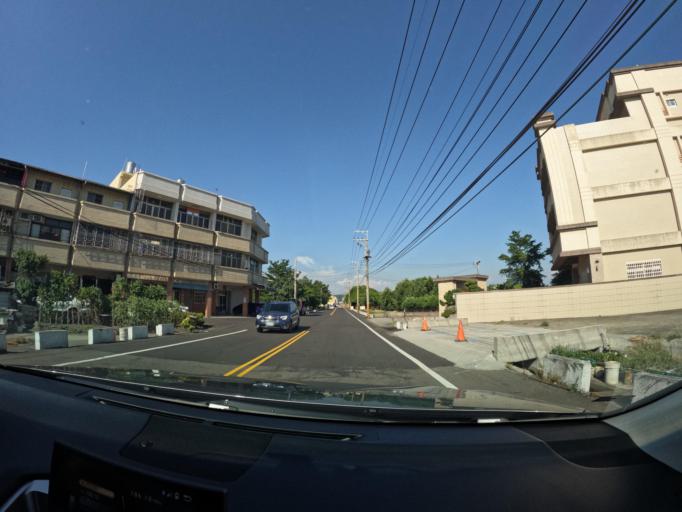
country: TW
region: Taiwan
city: Fengyuan
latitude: 24.2653
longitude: 120.5524
